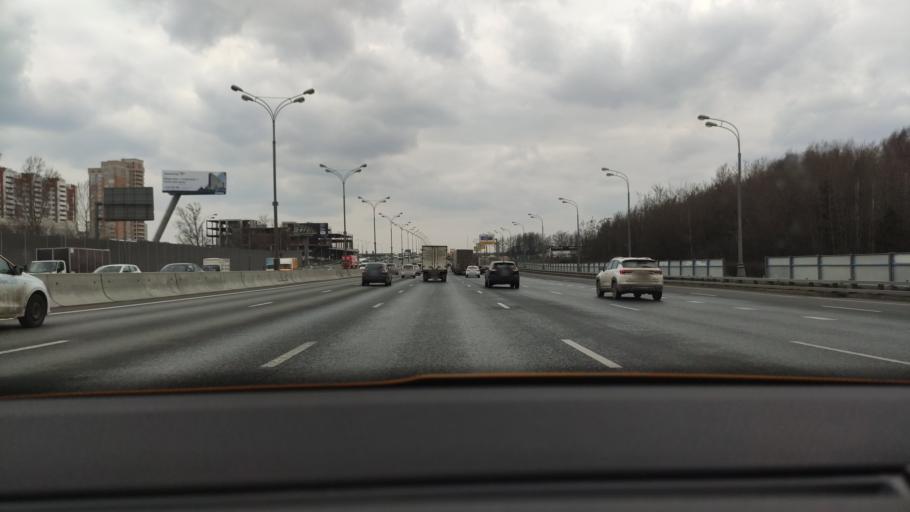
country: RU
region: Moscow
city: Vagonoremont
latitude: 55.9079
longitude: 37.5569
